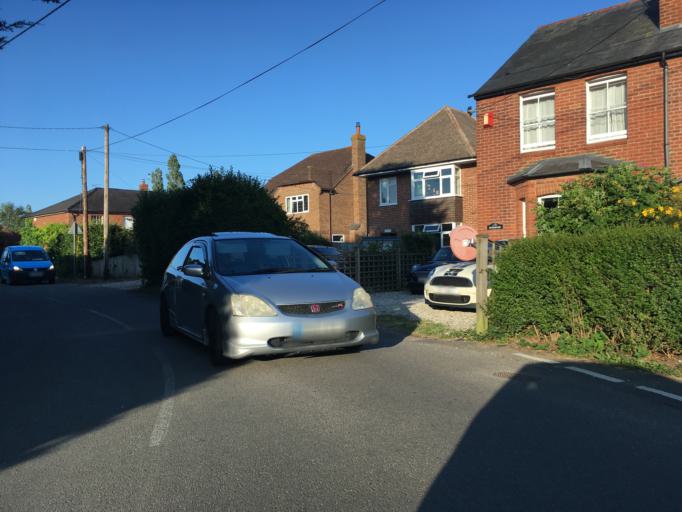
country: GB
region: England
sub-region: Hampshire
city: Tadley
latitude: 51.4163
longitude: -1.1477
